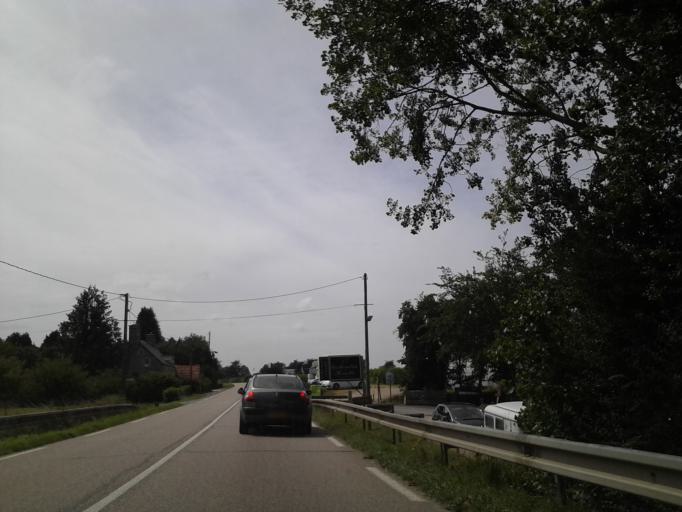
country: FR
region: Lower Normandy
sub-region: Departement de la Manche
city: Valognes
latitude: 49.5003
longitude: -1.5014
